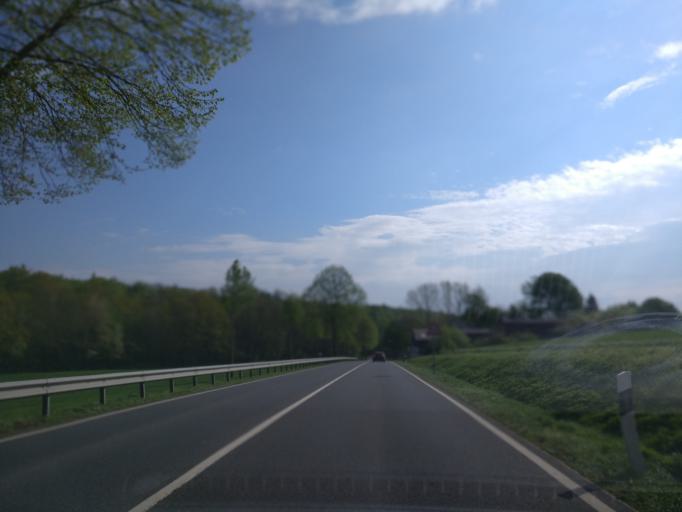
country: DE
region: Lower Saxony
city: Juhnde
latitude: 51.5153
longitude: 9.8113
